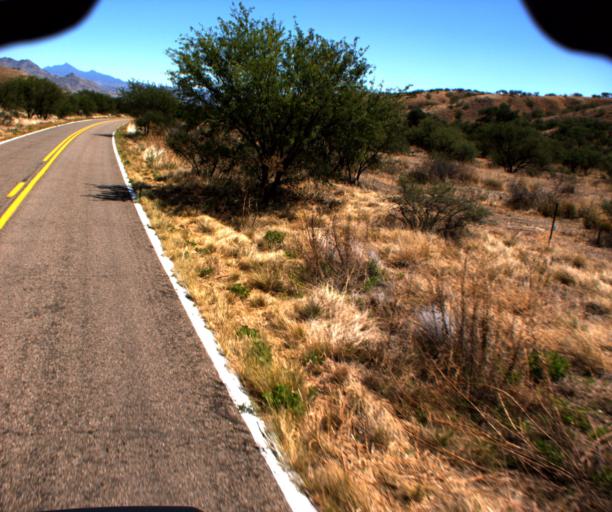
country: US
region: Arizona
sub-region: Santa Cruz County
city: Rio Rico
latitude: 31.4088
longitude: -111.0233
